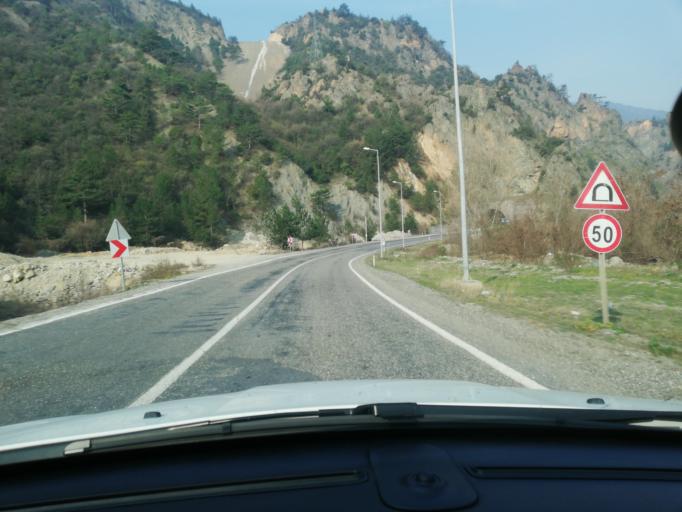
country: TR
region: Karabuk
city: Karabuk
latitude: 41.1518
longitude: 32.5315
